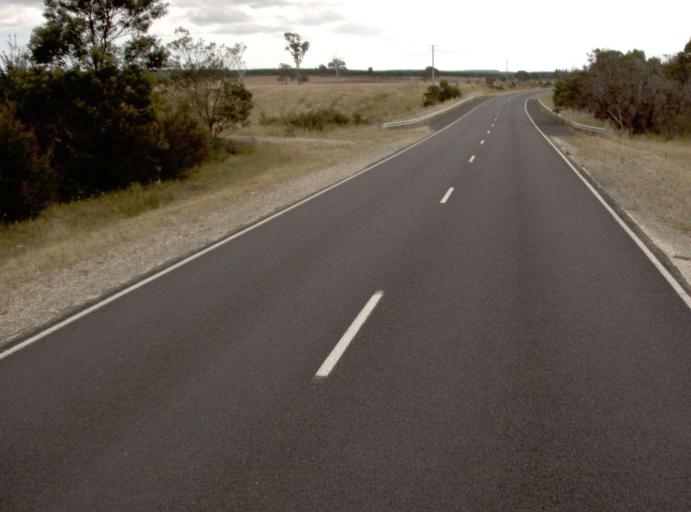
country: AU
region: Victoria
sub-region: Wellington
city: Sale
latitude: -38.1651
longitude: 147.0682
